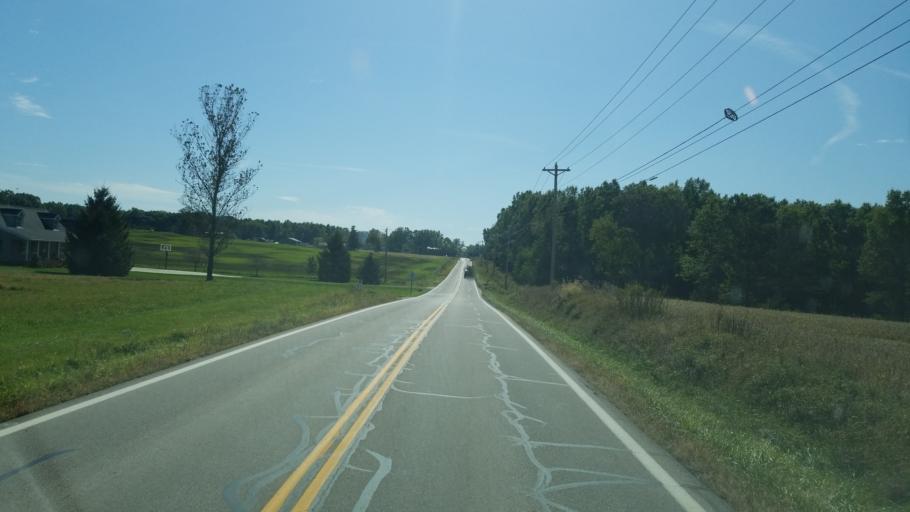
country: US
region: Ohio
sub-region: Wayne County
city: West Salem
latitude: 40.8873
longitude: -82.1086
